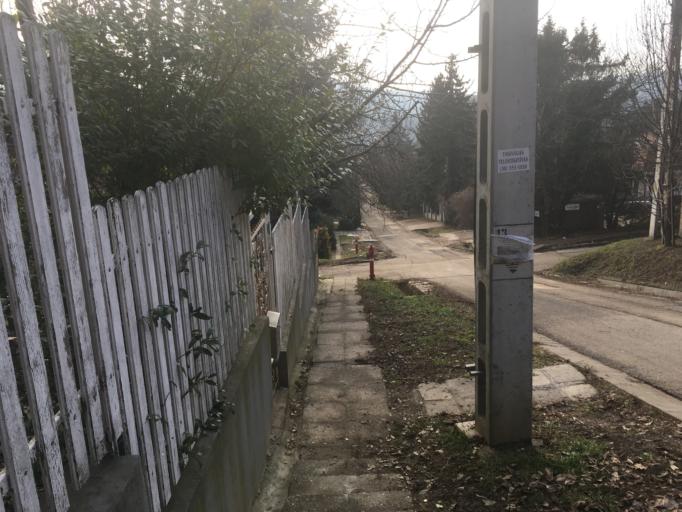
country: HU
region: Pest
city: Solymar
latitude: 47.5498
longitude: 18.9701
